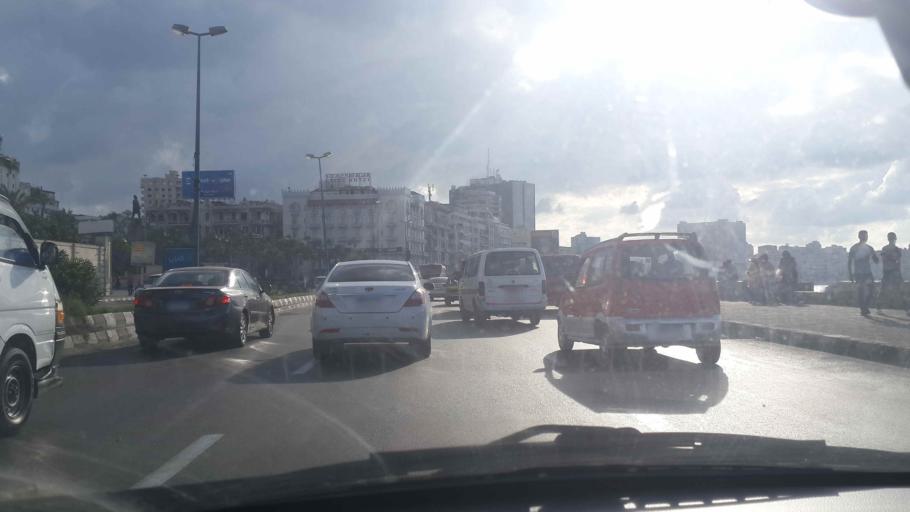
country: EG
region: Alexandria
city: Alexandria
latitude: 31.2021
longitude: 29.9006
